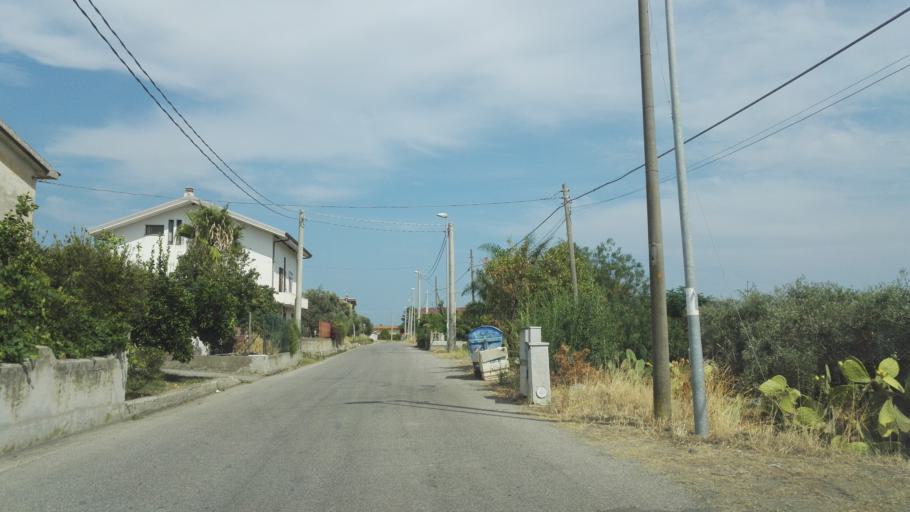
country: IT
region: Calabria
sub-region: Provincia di Reggio Calabria
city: Monasterace
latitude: 38.4272
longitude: 16.5426
